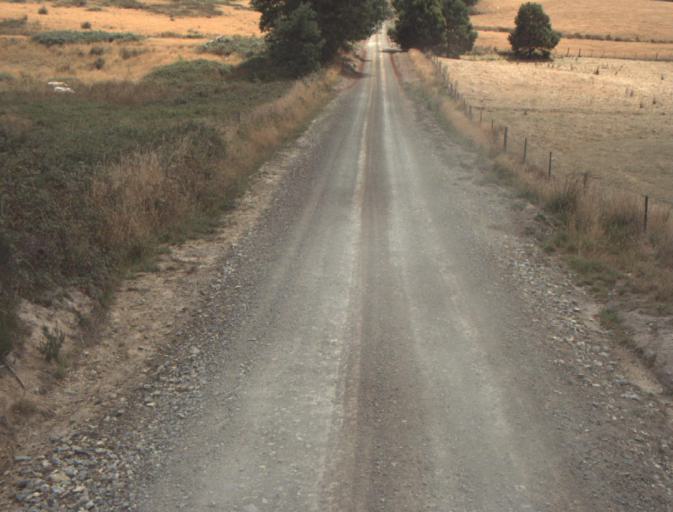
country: AU
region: Tasmania
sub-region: Launceston
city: Mayfield
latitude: -41.1977
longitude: 147.1695
